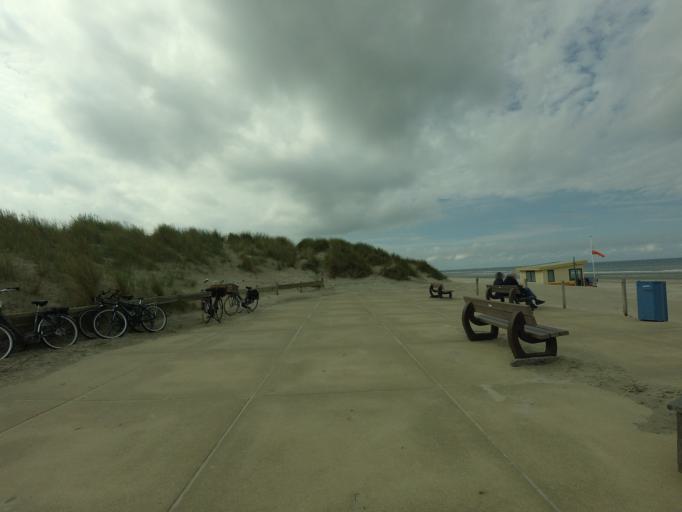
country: NL
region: Friesland
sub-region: Gemeente Ameland
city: Nes
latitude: 53.4614
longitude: 5.8080
